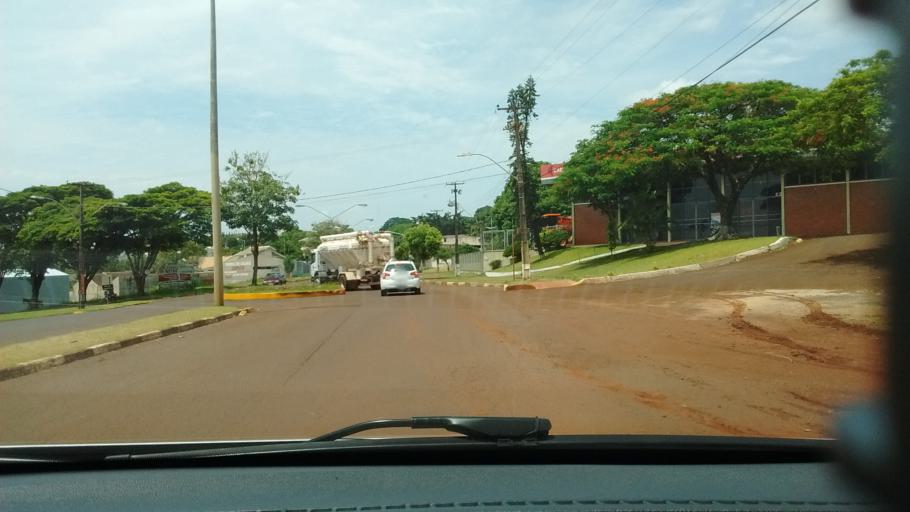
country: BR
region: Parana
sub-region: Corbelia
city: Corbelia
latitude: -24.5515
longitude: -52.9935
